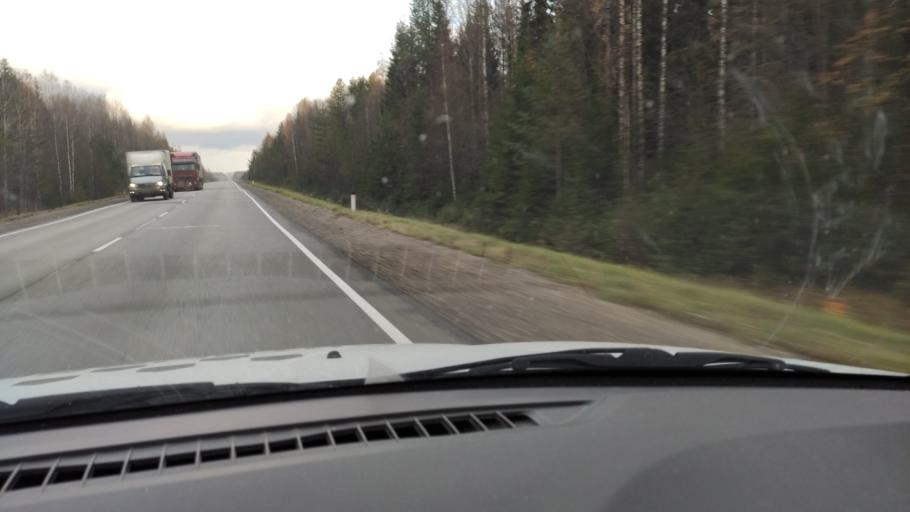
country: RU
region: Kirov
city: Chernaya Kholunitsa
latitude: 58.8145
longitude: 51.8255
